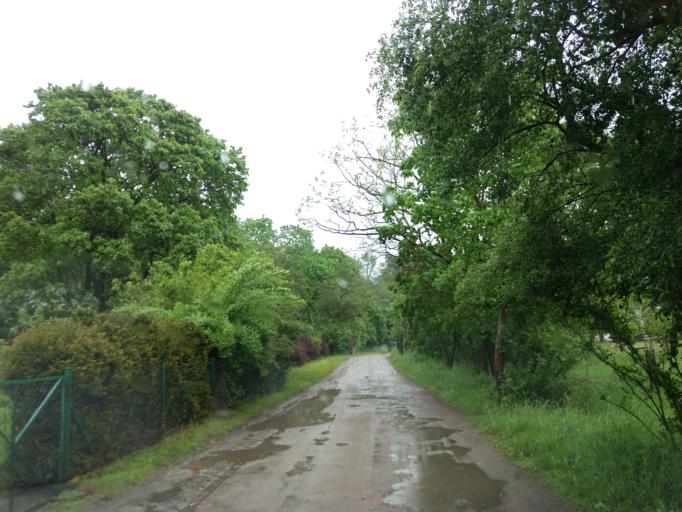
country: PL
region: Greater Poland Voivodeship
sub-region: Powiat czarnkowsko-trzcianecki
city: Krzyz Wielkopolski
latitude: 53.0460
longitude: 15.9444
